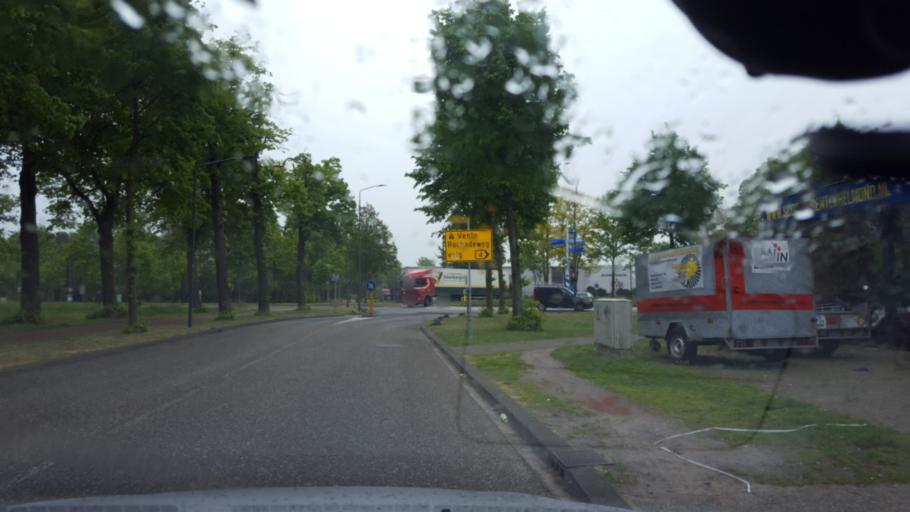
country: NL
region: North Brabant
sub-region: Gemeente Helmond
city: Helmond
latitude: 51.4670
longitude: 5.6887
